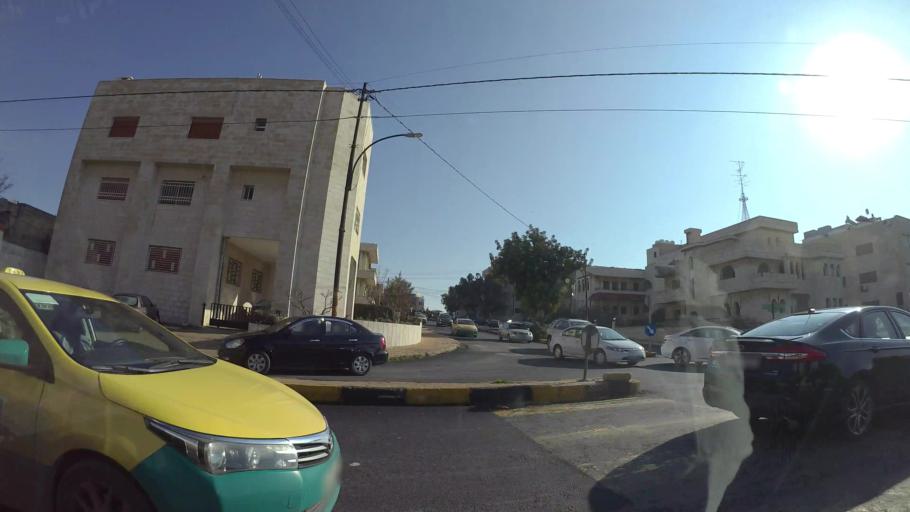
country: JO
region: Amman
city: Al Jubayhah
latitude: 32.0010
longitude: 35.8848
